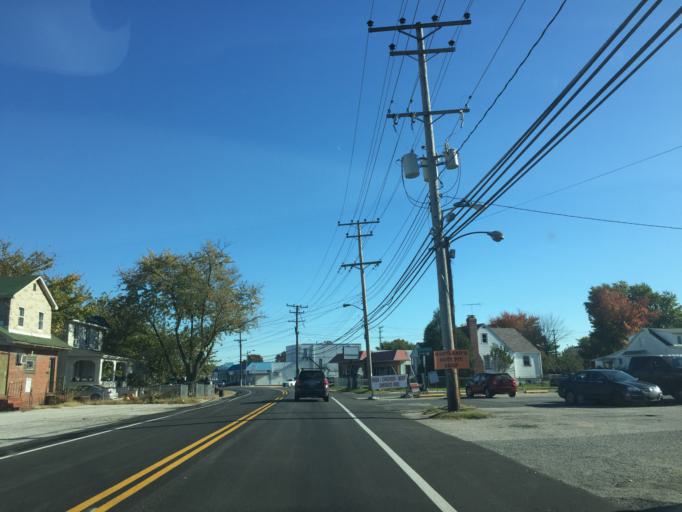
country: US
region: Maryland
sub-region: Baltimore County
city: Essex
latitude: 39.2802
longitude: -76.4912
